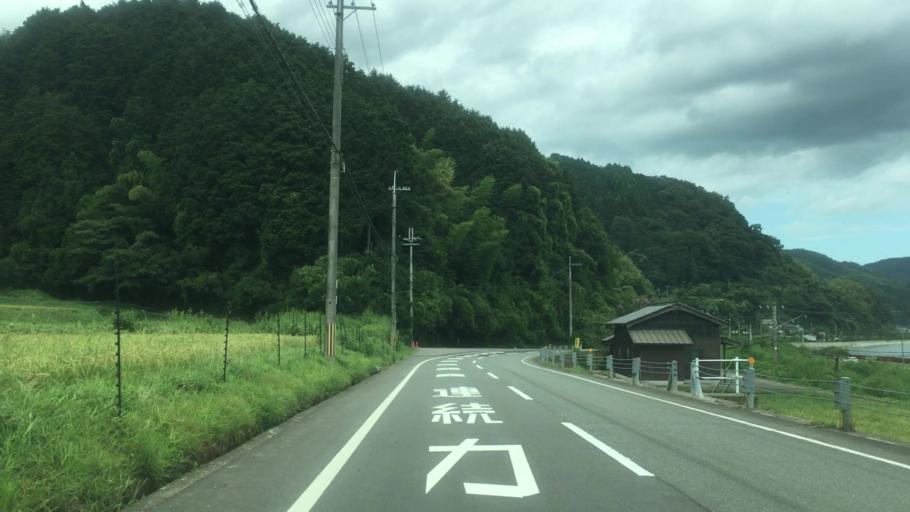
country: JP
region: Hyogo
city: Toyooka
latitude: 35.5786
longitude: 134.8004
